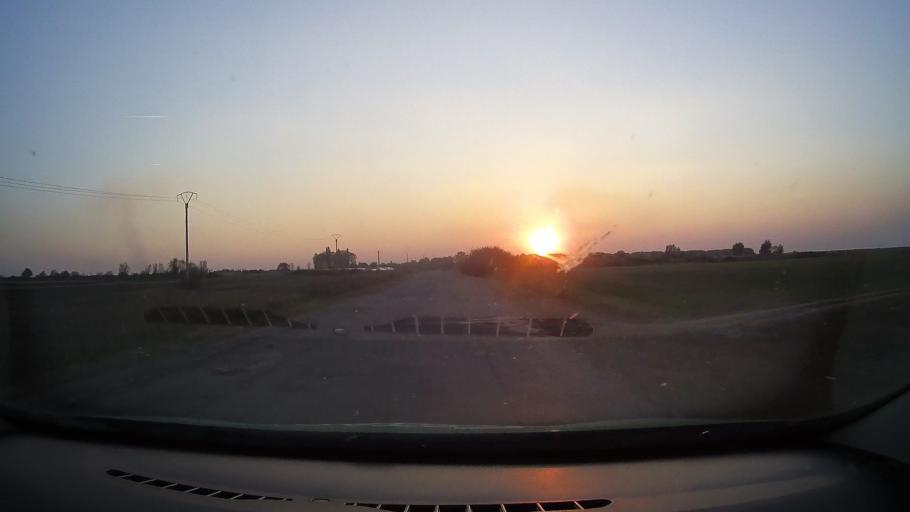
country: RO
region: Arad
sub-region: Comuna Olari
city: Olari
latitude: 46.4040
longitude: 21.5778
